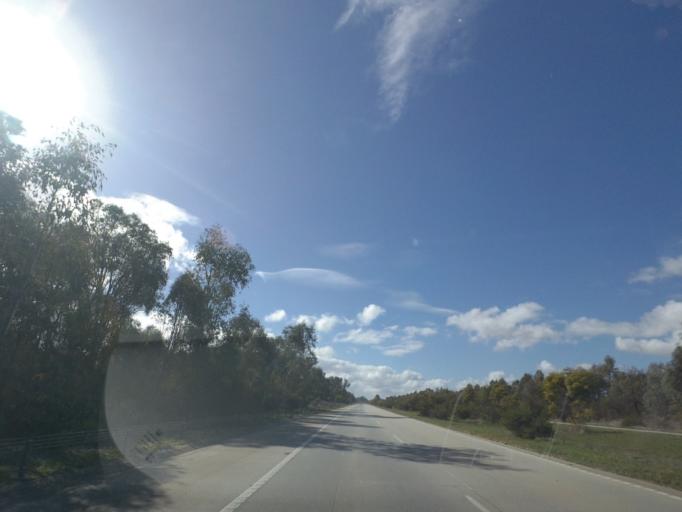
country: AU
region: New South Wales
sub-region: Albury Municipality
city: Lavington
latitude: -36.0258
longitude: 146.9791
